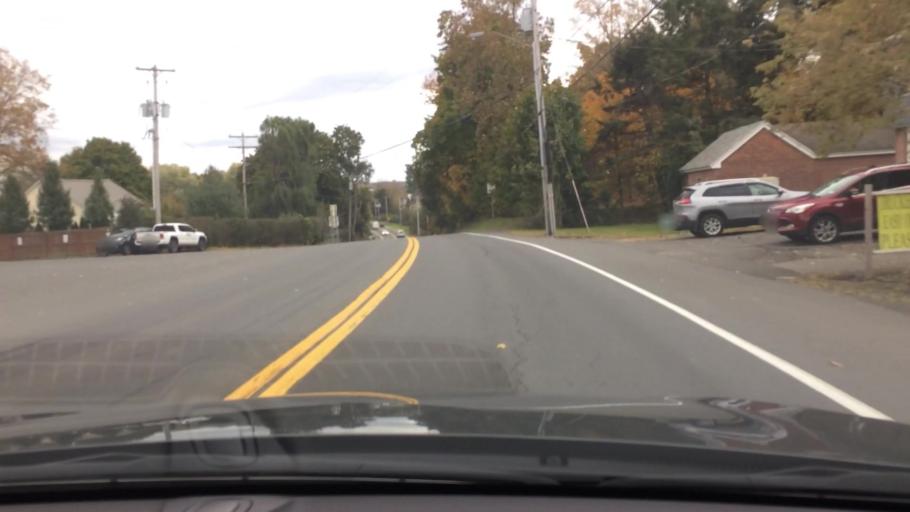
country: US
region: New York
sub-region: Columbia County
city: Lorenz Park
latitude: 42.2220
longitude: -73.7348
